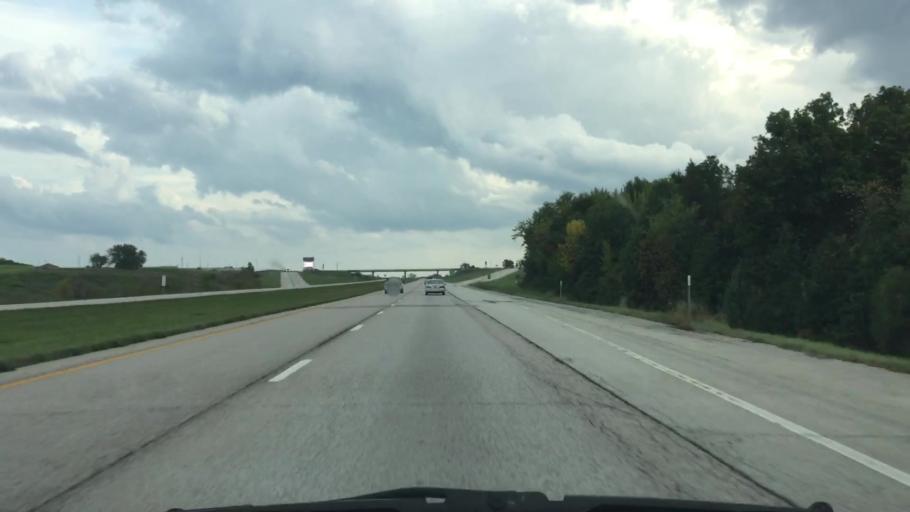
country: US
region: Missouri
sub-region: Clinton County
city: Cameron
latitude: 39.7367
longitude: -94.2205
